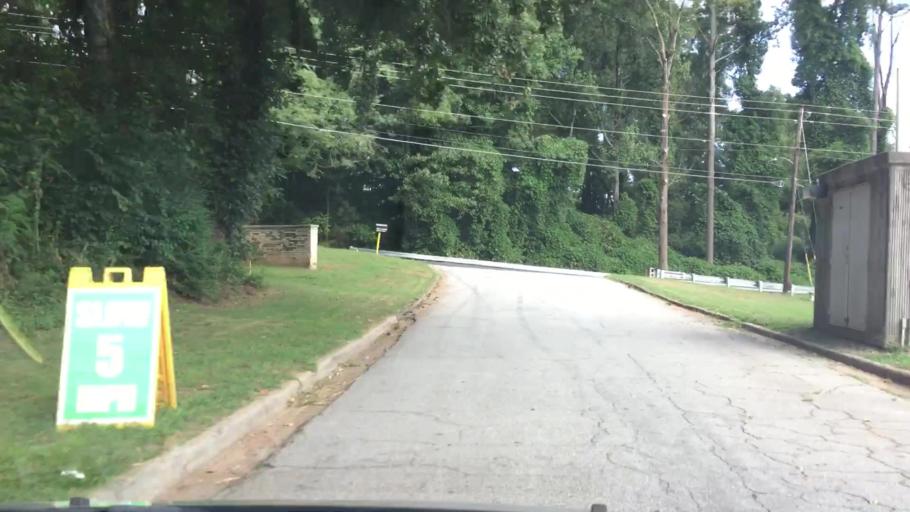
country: US
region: Georgia
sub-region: DeKalb County
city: Gresham Park
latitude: 33.7018
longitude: -84.3324
